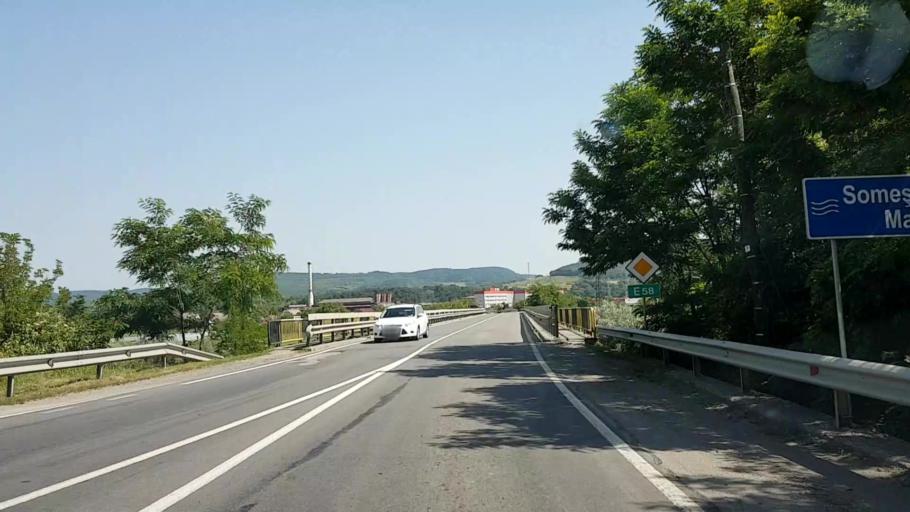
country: RO
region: Bistrita-Nasaud
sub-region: Comuna Beclean
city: Beclean
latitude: 47.1780
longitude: 24.1472
